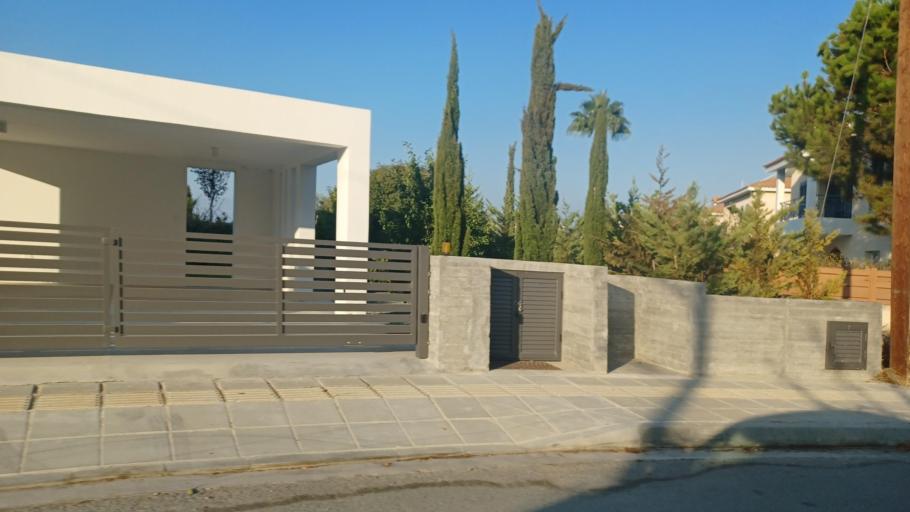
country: CY
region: Pafos
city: Paphos
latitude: 34.7838
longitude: 32.4529
